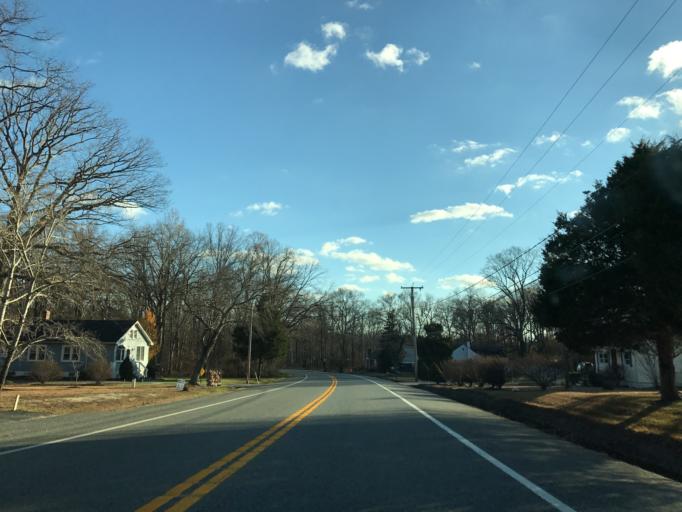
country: US
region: Maryland
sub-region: Harford County
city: Edgewood
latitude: 39.4097
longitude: -76.3238
